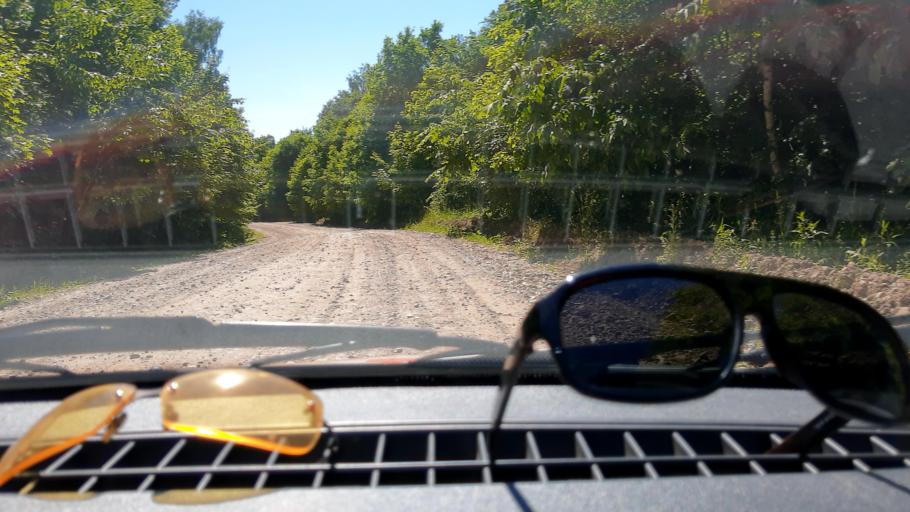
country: RU
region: Bashkortostan
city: Ulu-Telyak
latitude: 54.8011
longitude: 57.0298
